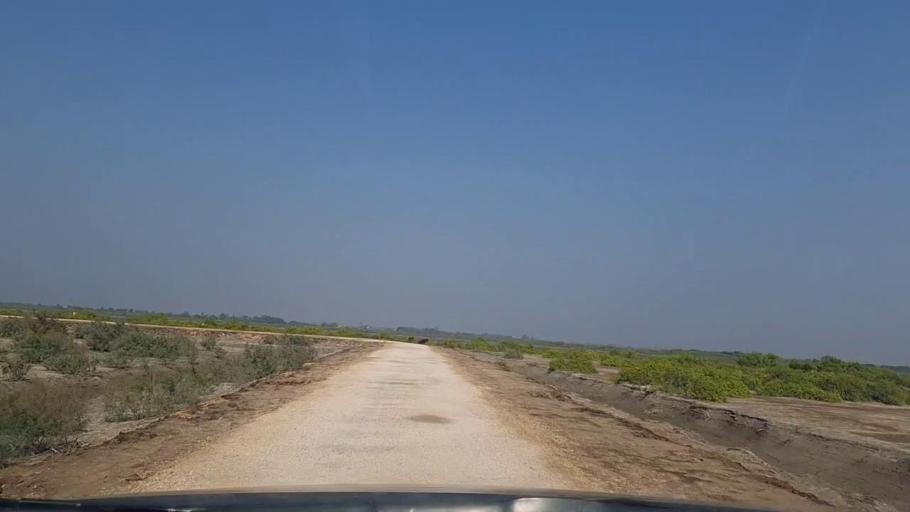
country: PK
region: Sindh
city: Mirpur Sakro
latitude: 24.5780
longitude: 67.7576
